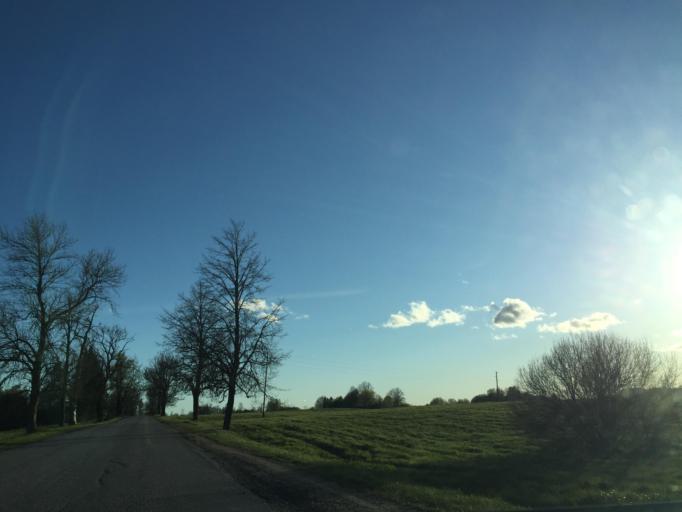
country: LV
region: Vecpiebalga
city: Vecpiebalga
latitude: 56.8636
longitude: 25.8657
